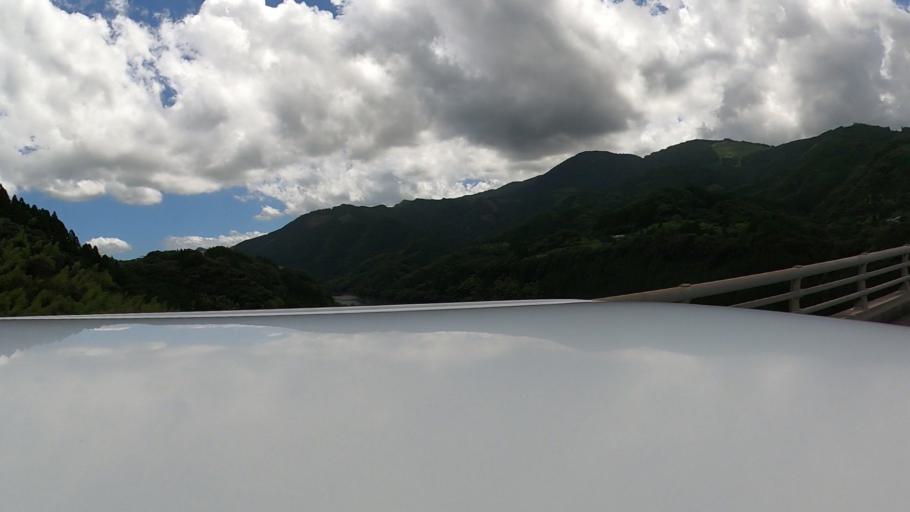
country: JP
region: Miyazaki
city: Nobeoka
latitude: 32.5952
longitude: 131.4946
